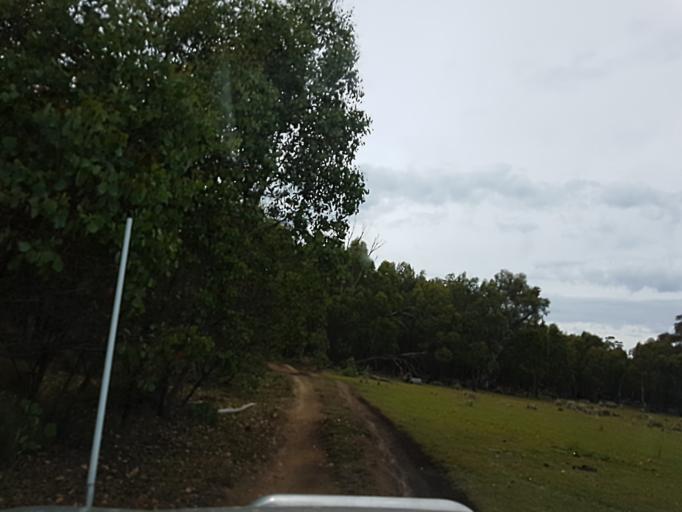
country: AU
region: New South Wales
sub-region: Snowy River
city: Jindabyne
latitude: -36.8549
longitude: 148.2617
